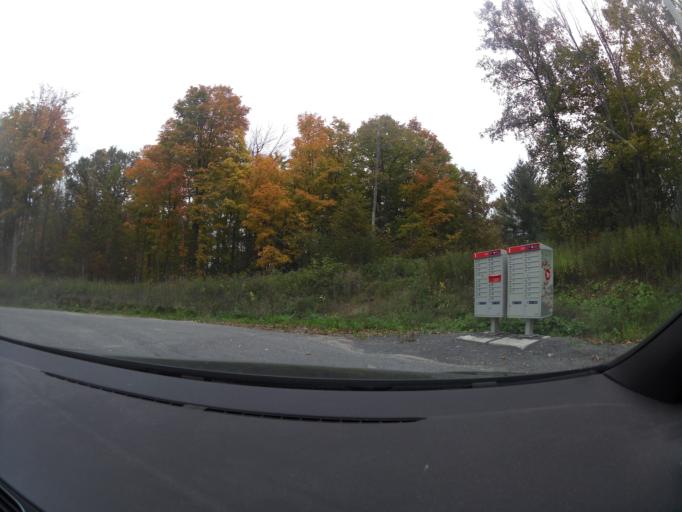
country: CA
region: Ontario
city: Bells Corners
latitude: 45.3778
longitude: -75.9730
